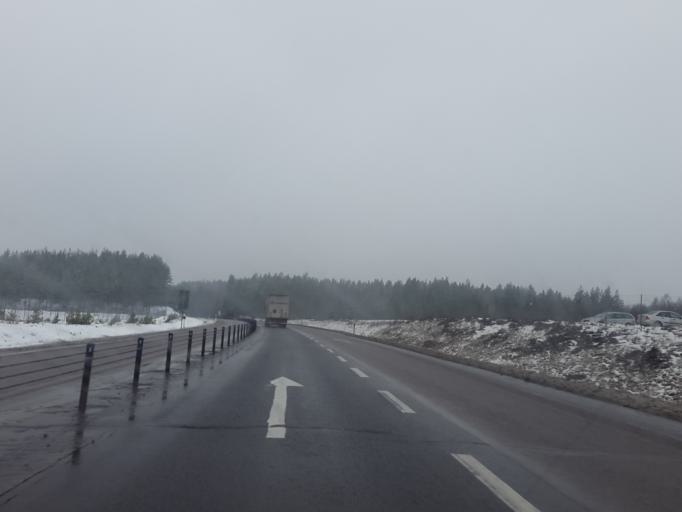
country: SE
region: Joenkoeping
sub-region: Jonkopings Kommun
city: Jonkoping
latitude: 57.7731
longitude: 14.0779
